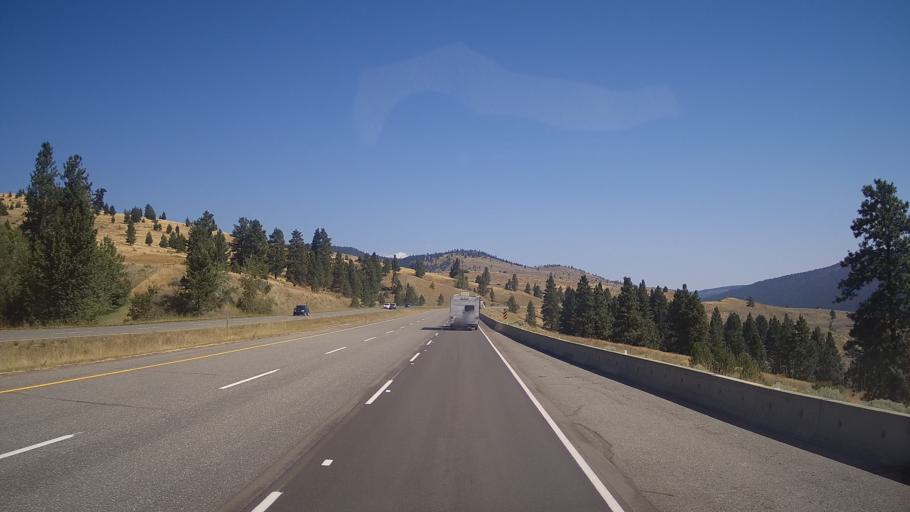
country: CA
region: British Columbia
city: Merritt
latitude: 50.1752
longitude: -120.6944
